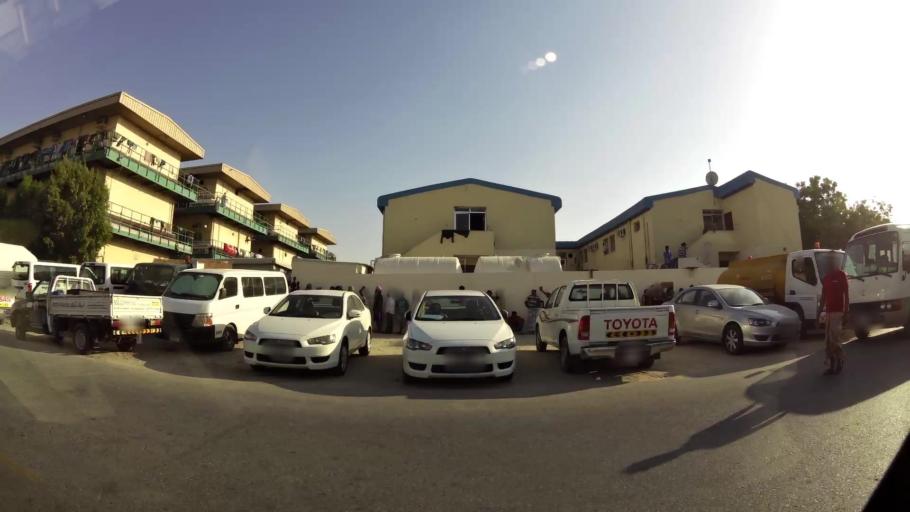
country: AE
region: Dubai
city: Dubai
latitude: 25.1276
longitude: 55.2379
